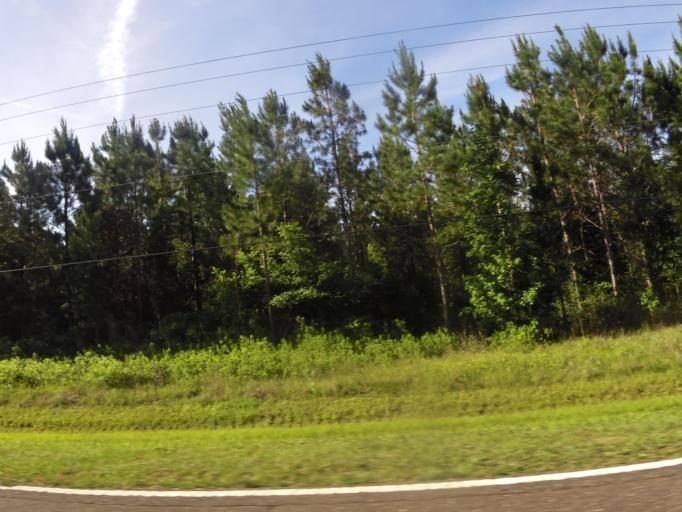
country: US
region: Florida
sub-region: Nassau County
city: Nassau Village-Ratliff
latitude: 30.4651
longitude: -81.7971
